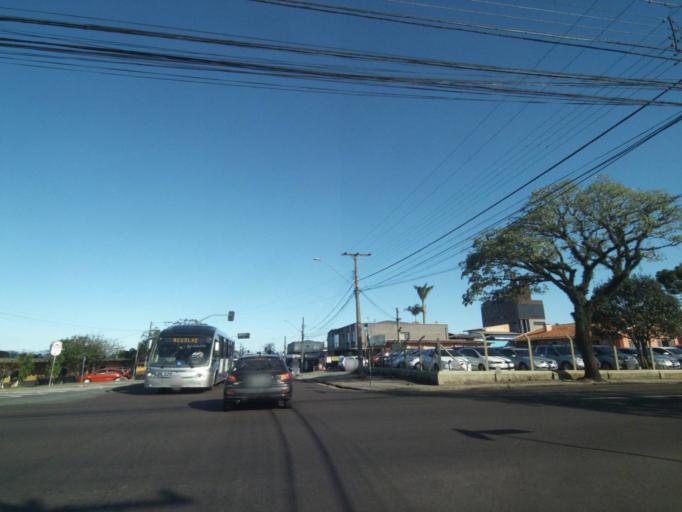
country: BR
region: Parana
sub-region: Curitiba
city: Curitiba
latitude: -25.3932
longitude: -49.2418
